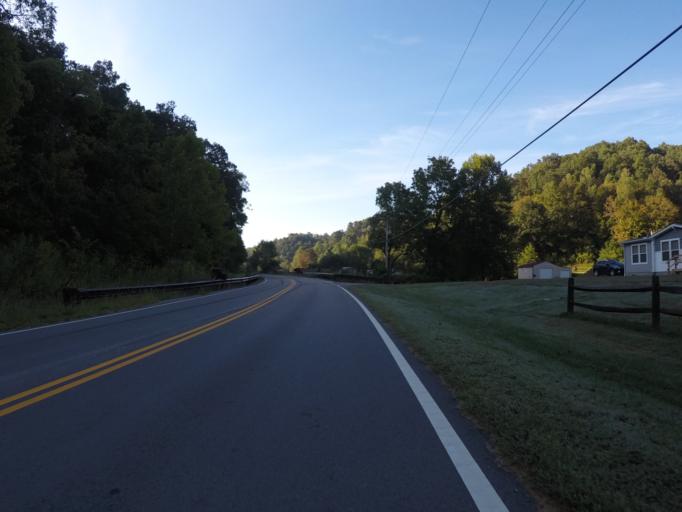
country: US
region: Ohio
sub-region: Lawrence County
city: Ironton
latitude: 38.6116
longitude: -82.5911
